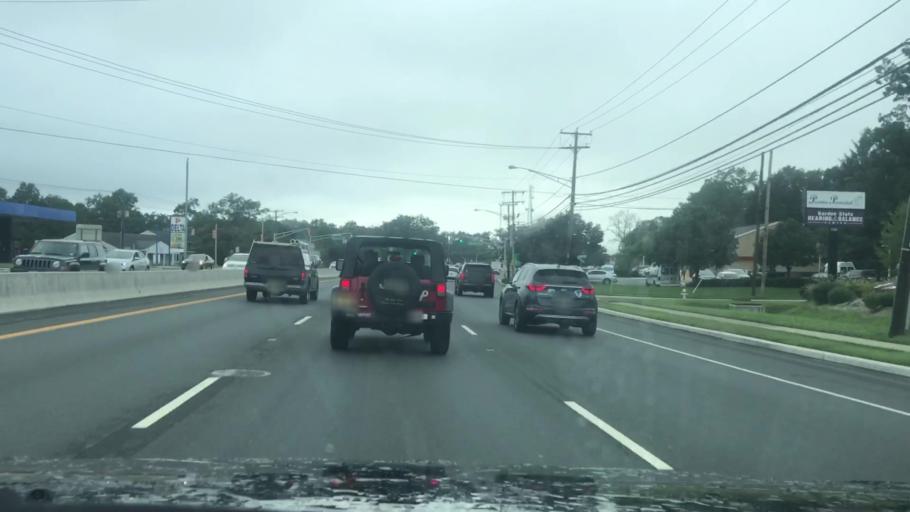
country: US
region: New Jersey
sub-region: Ocean County
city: Silver Ridge
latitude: 39.9672
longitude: -74.2271
